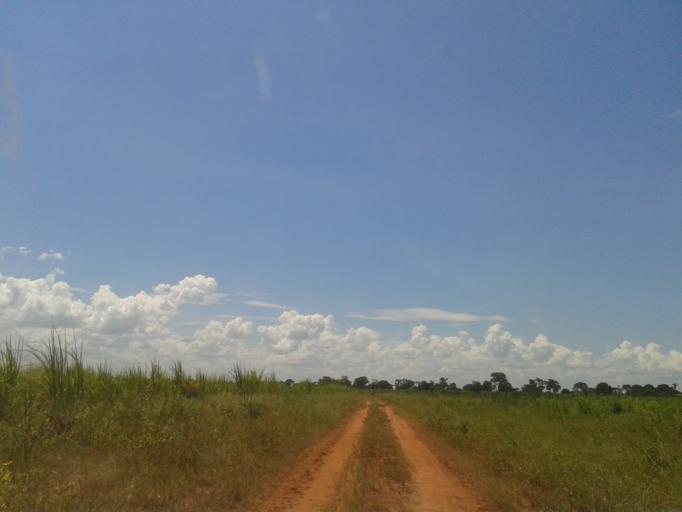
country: BR
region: Minas Gerais
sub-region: Santa Vitoria
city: Santa Vitoria
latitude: -19.1763
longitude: -50.4508
